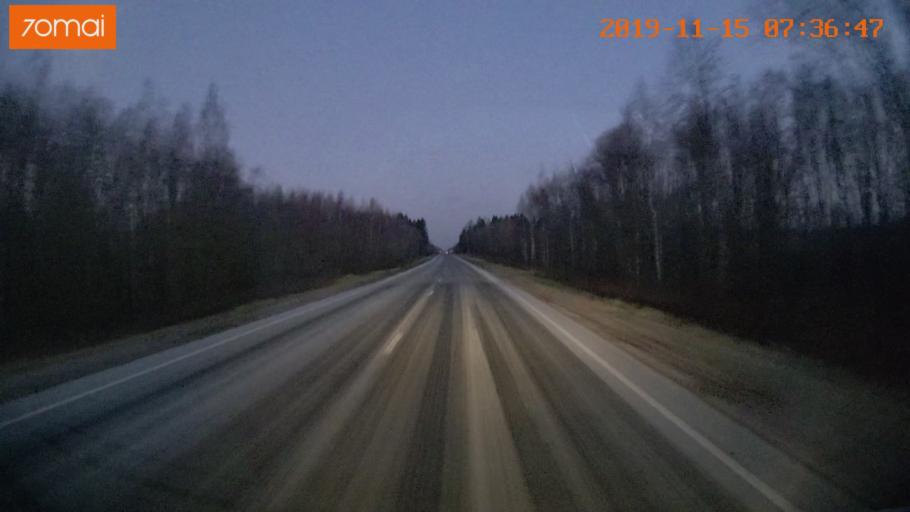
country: RU
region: Vologda
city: Sheksna
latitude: 58.7429
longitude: 38.4290
